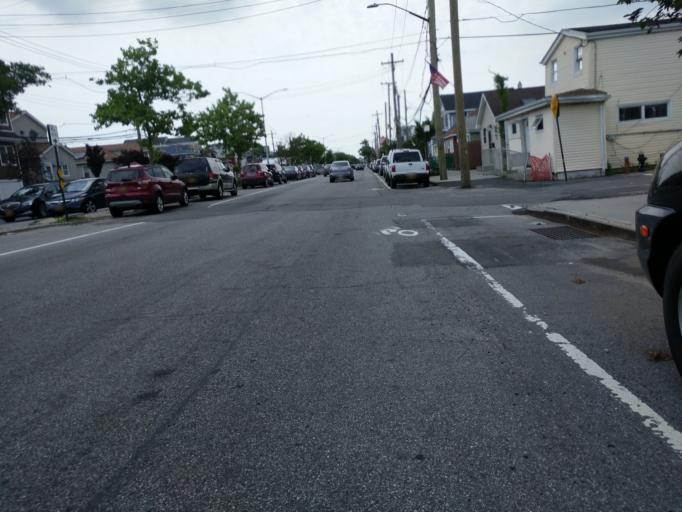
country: US
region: New York
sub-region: Nassau County
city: Inwood
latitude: 40.6046
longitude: -73.8199
